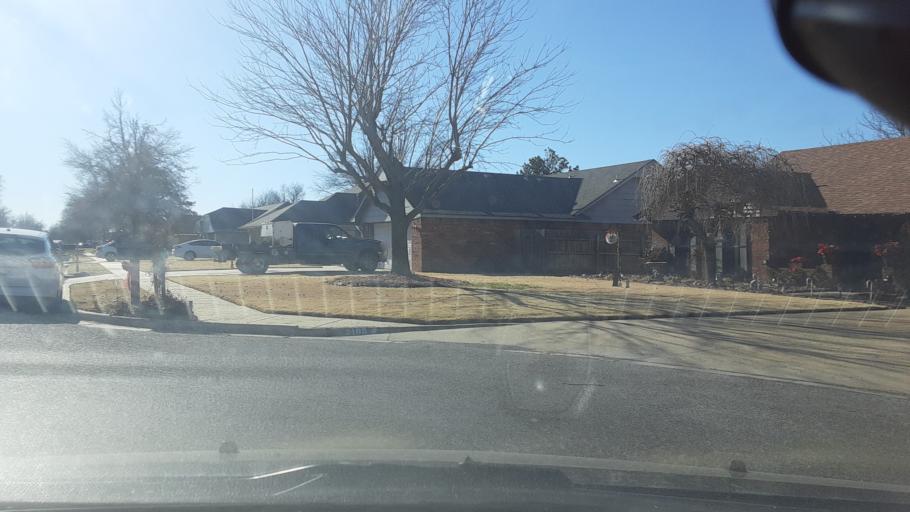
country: US
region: Oklahoma
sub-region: Kay County
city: Ponca City
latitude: 36.7311
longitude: -97.0892
